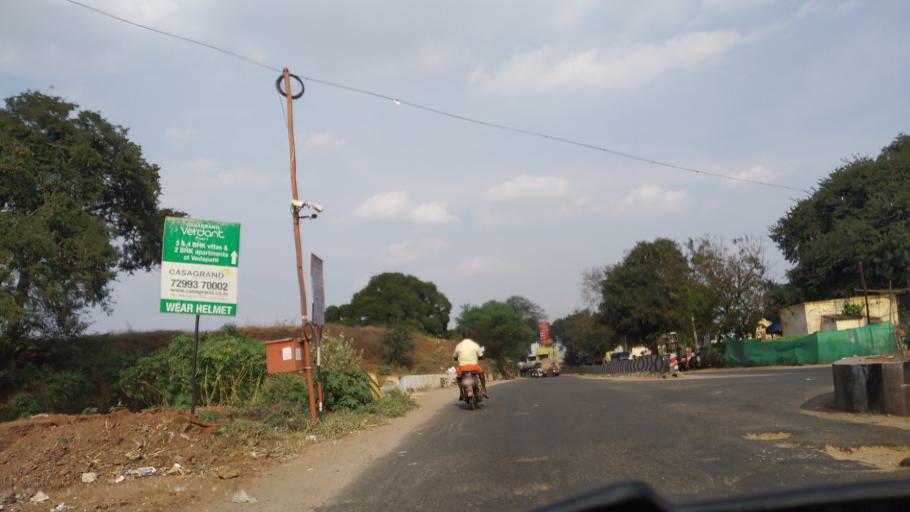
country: IN
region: Tamil Nadu
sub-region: Coimbatore
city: Perur
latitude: 10.9709
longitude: 76.9111
